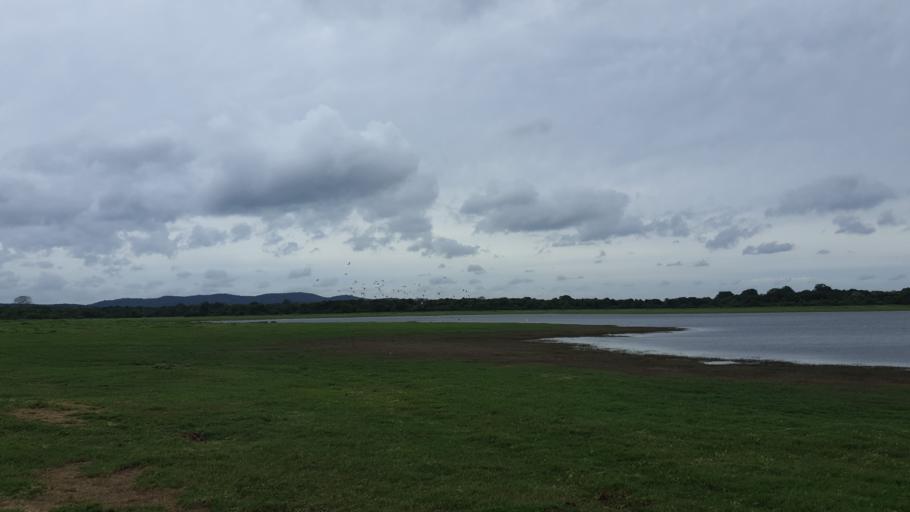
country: LK
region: North Central
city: Polonnaruwa
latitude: 8.1326
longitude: 80.9114
